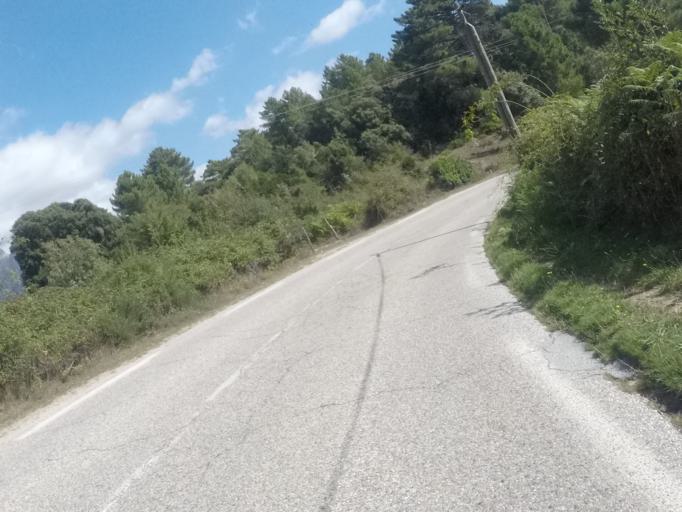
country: FR
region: Corsica
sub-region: Departement de la Corse-du-Sud
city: Zonza
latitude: 41.7594
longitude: 9.1837
